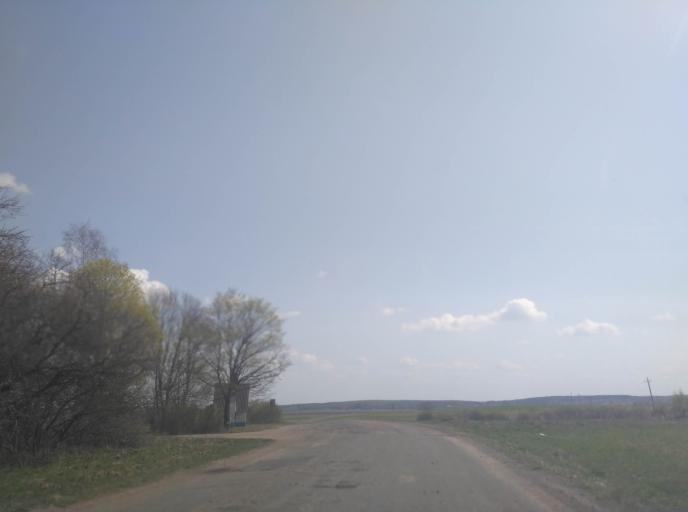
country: BY
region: Minsk
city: Loshnitsa
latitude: 54.4912
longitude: 28.7249
